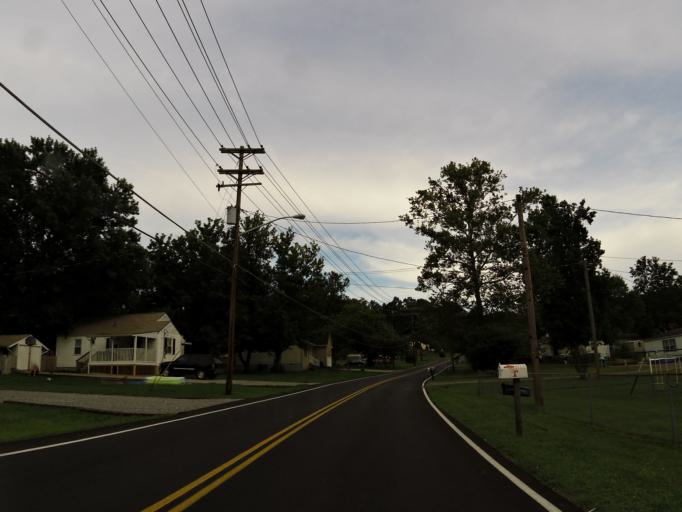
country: US
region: Tennessee
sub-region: Knox County
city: Knoxville
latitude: 36.0150
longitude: -83.8997
